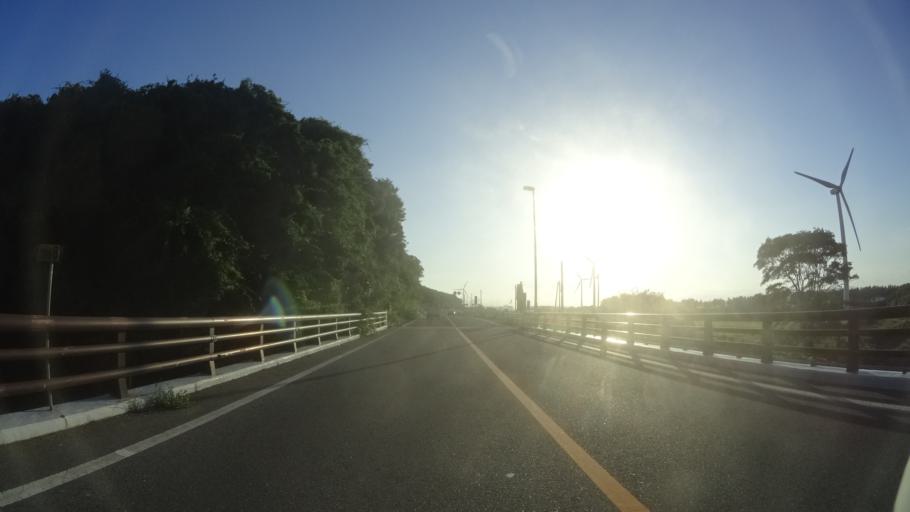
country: JP
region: Tottori
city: Yonago
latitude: 35.4959
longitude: 133.4597
